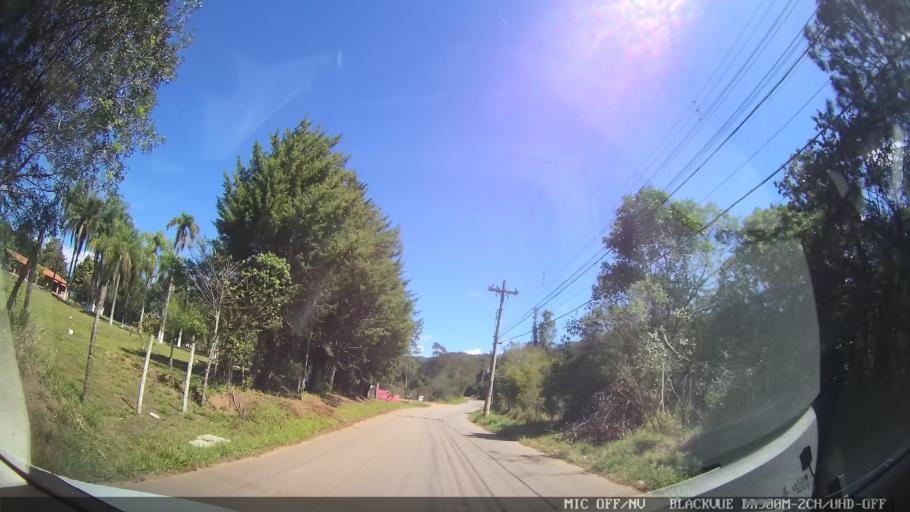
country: BR
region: Sao Paulo
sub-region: Jarinu
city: Jarinu
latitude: -23.1624
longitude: -46.7326
